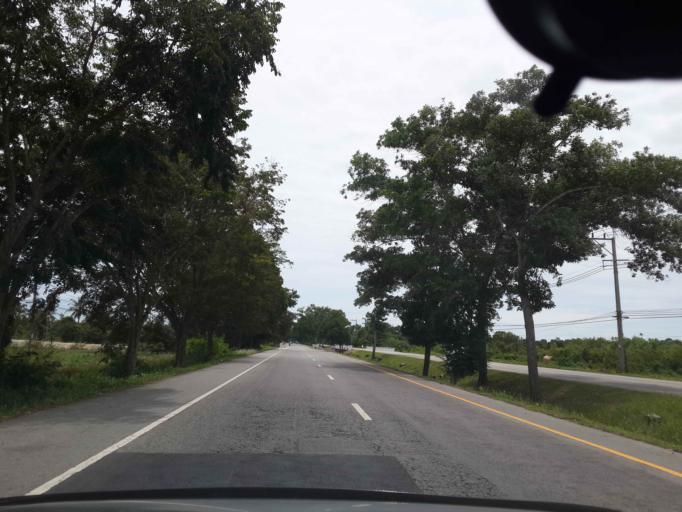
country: TH
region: Narathiwat
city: Yi-ngo
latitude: 6.4040
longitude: 101.7295
